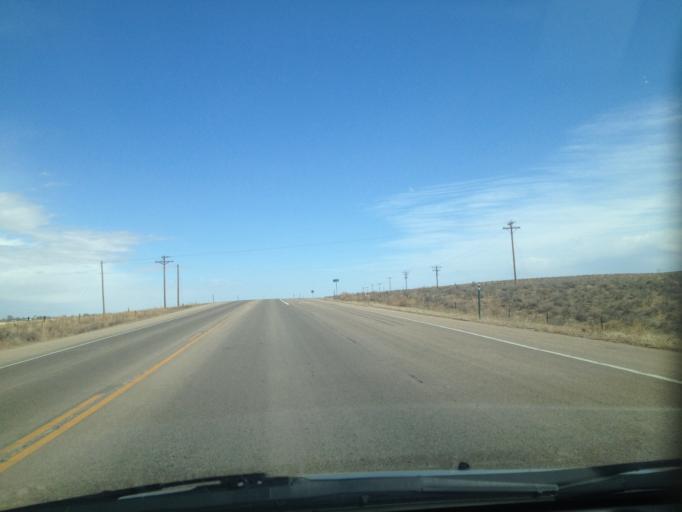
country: US
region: Colorado
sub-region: Weld County
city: Kersey
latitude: 40.2936
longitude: -104.2931
